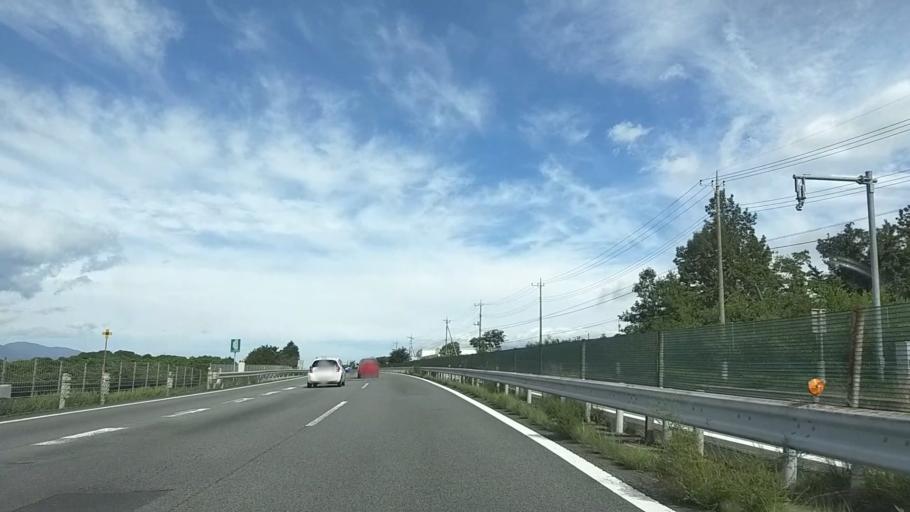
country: JP
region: Yamanashi
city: Nirasaki
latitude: 35.7120
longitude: 138.4724
